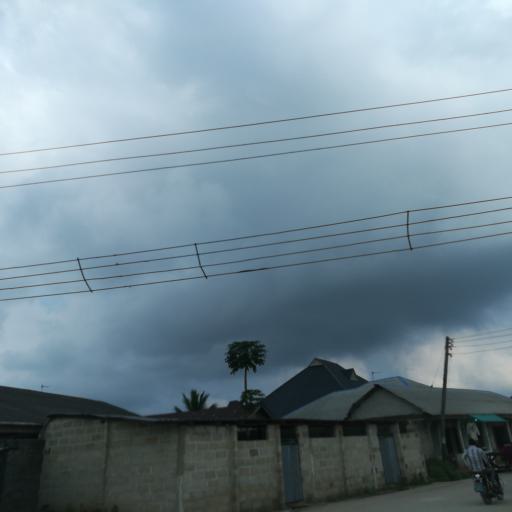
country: NG
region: Rivers
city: Okrika
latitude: 4.8014
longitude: 7.1241
